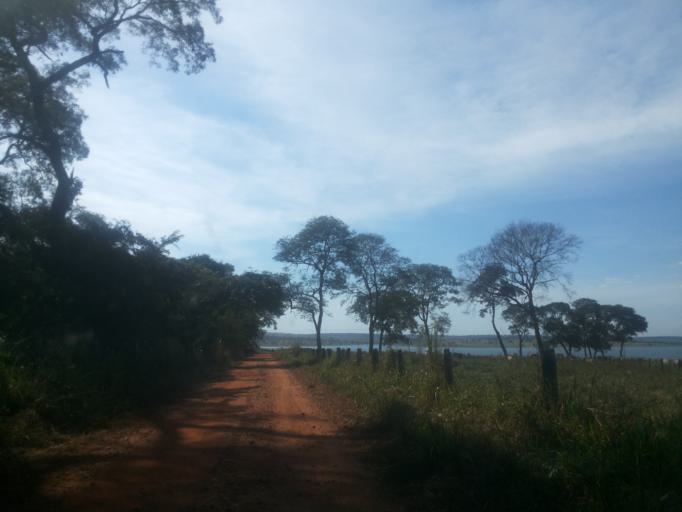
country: BR
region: Minas Gerais
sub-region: Santa Vitoria
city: Santa Vitoria
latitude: -19.0080
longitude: -50.4016
